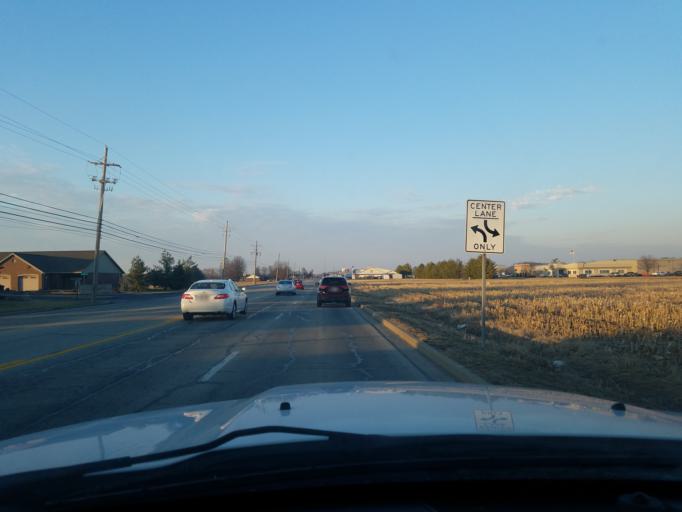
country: US
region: Indiana
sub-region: Vanderburgh County
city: Melody Hill
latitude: 38.0049
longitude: -87.4738
